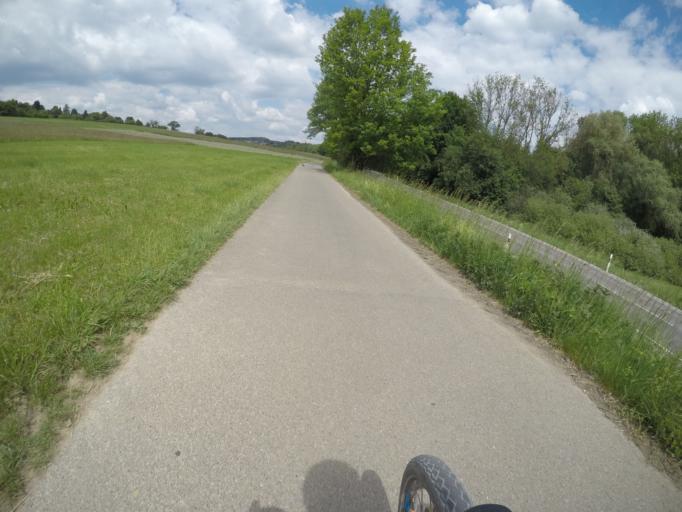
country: DE
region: Baden-Wuerttemberg
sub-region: Regierungsbezirk Stuttgart
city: Ostfildern
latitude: 48.7207
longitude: 9.2179
